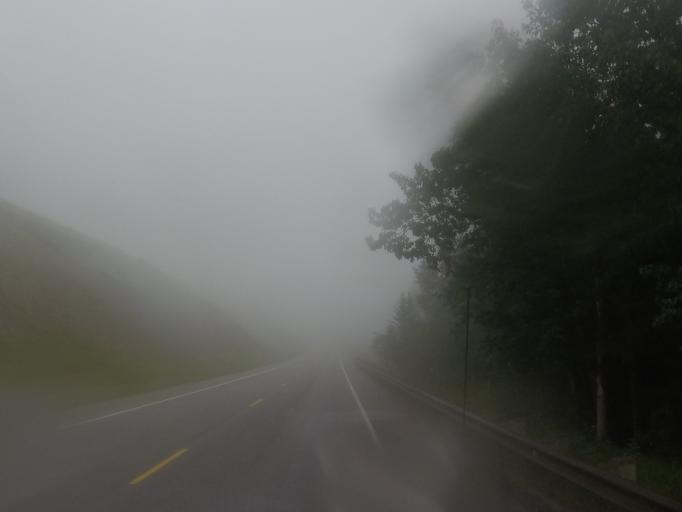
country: US
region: Wyoming
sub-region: Johnson County
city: Buffalo
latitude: 44.3192
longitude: -106.9164
